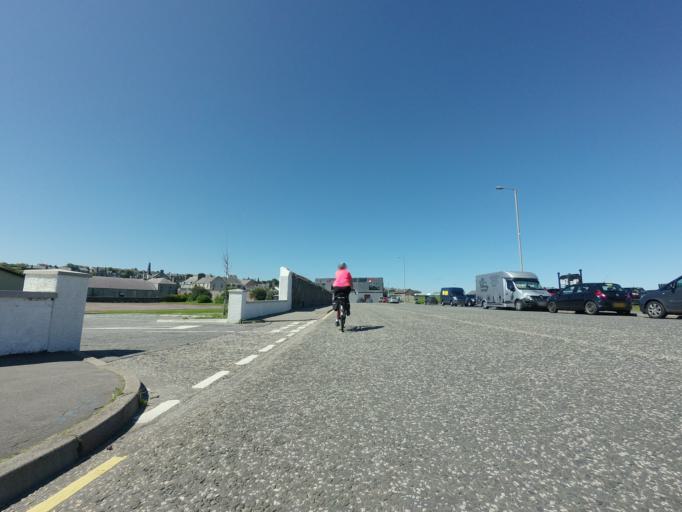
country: GB
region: Scotland
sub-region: Aberdeenshire
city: Banff
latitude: 57.6642
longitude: -2.5158
